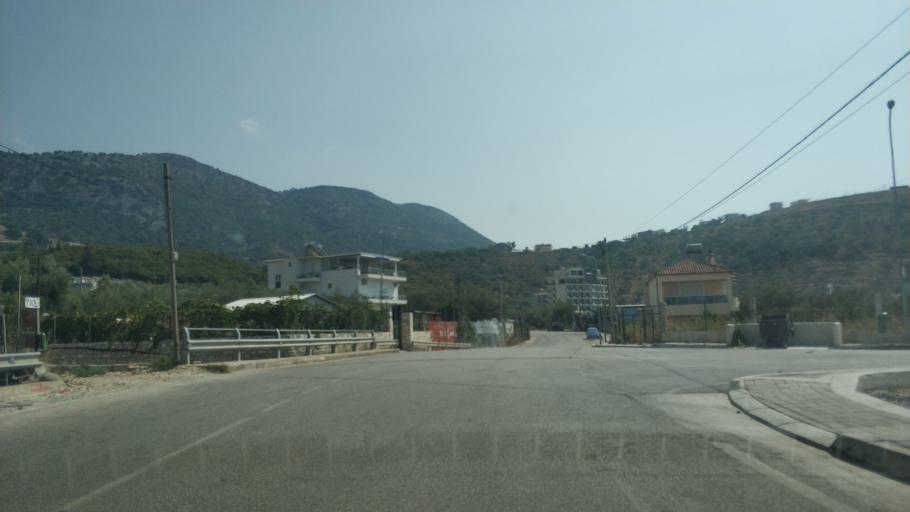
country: AL
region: Vlore
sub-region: Rrethi i Vlores
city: Himare
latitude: 40.0957
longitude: 19.7550
